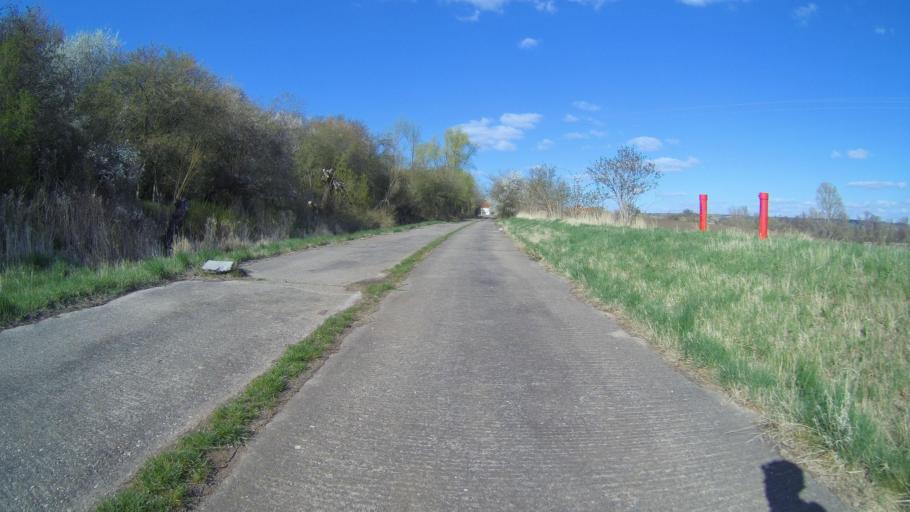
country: CZ
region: Ustecky
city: Brezno
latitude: 50.3582
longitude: 13.4190
